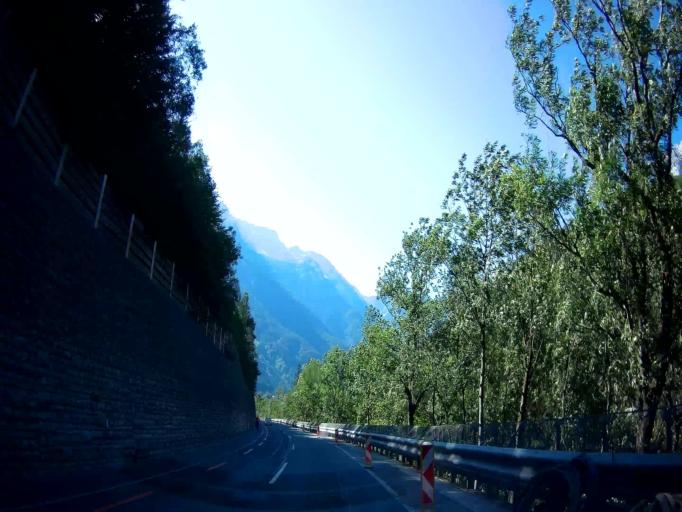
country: AT
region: Salzburg
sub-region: Politischer Bezirk Sankt Johann im Pongau
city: Werfen
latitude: 47.4876
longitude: 13.1840
